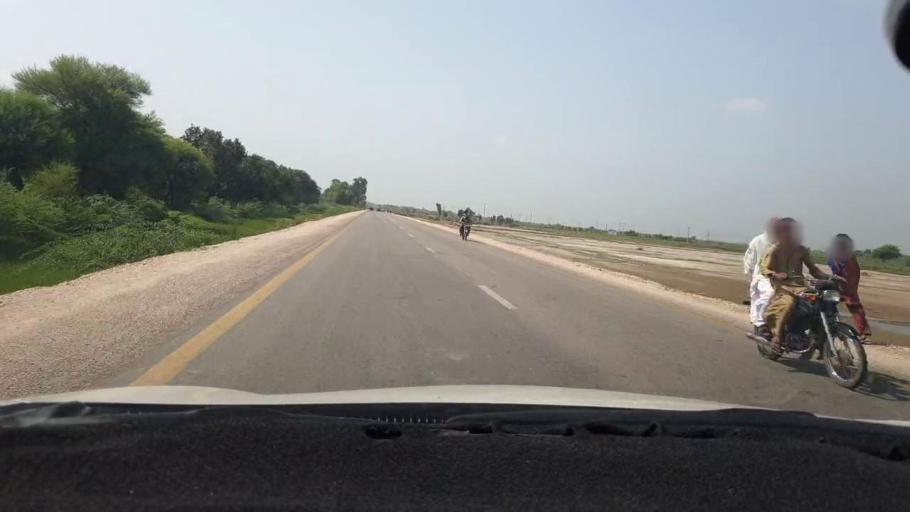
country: PK
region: Sindh
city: Mirpur Khas
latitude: 25.6803
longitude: 69.1104
